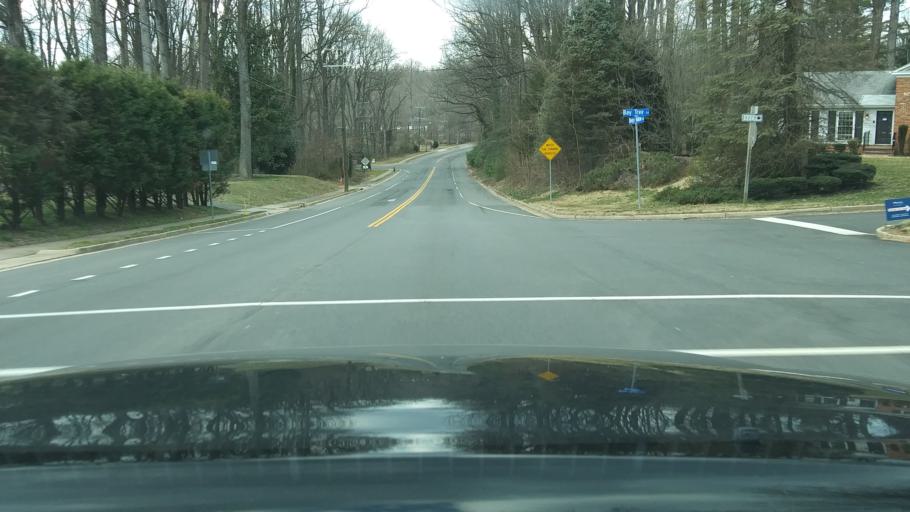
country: US
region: Virginia
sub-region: Fairfax County
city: Lake Barcroft
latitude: 38.8434
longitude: -77.1739
